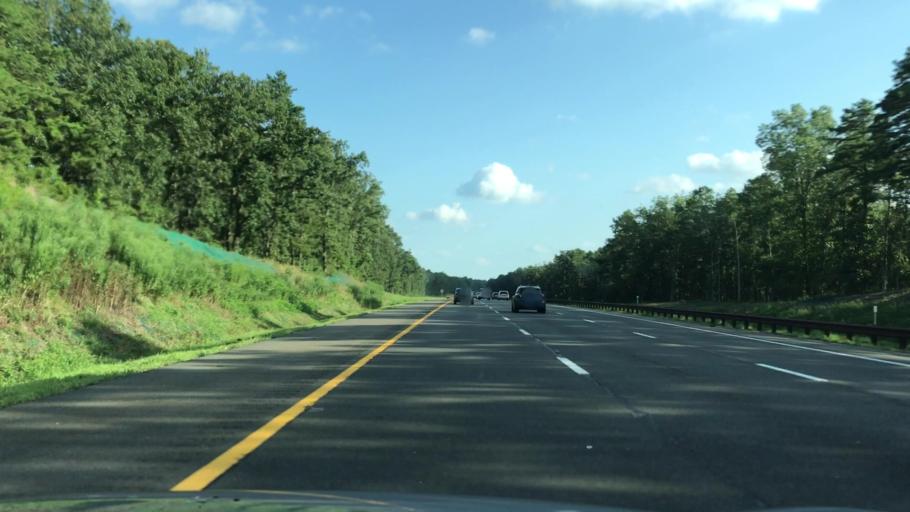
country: US
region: New Jersey
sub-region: Ocean County
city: Forked River
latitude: 39.8487
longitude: -74.2243
